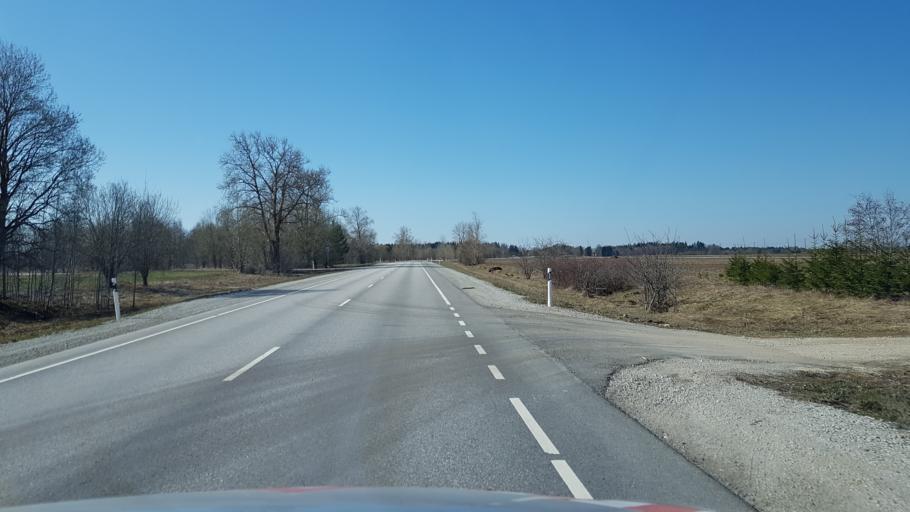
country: EE
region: Ida-Virumaa
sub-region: Kohtla-Jaerve linn
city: Kohtla-Jarve
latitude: 59.3190
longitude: 27.2533
